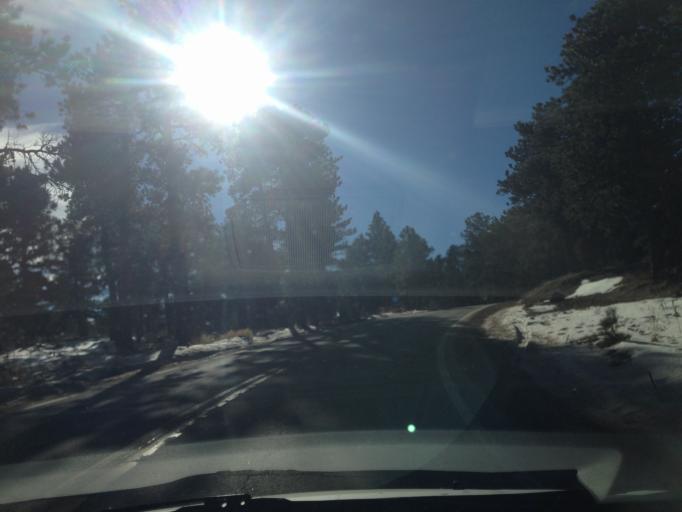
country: US
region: Colorado
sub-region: Boulder County
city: Boulder
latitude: 39.9900
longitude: -105.3197
